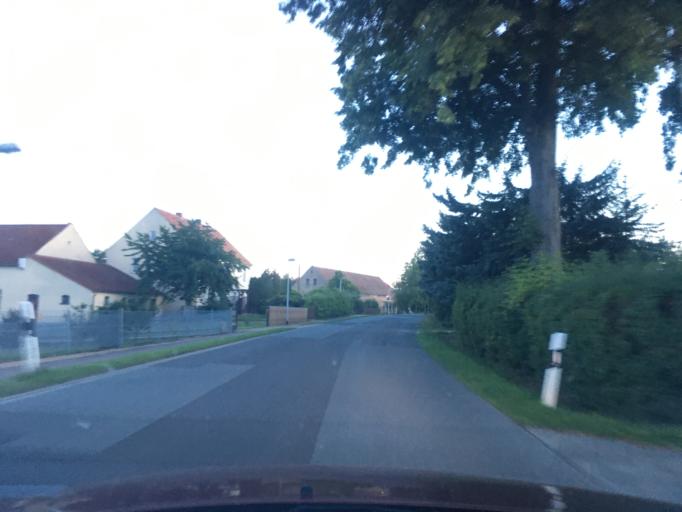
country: PL
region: Lower Silesian Voivodeship
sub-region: Powiat zgorzelecki
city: Piensk
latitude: 51.2311
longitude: 15.0100
